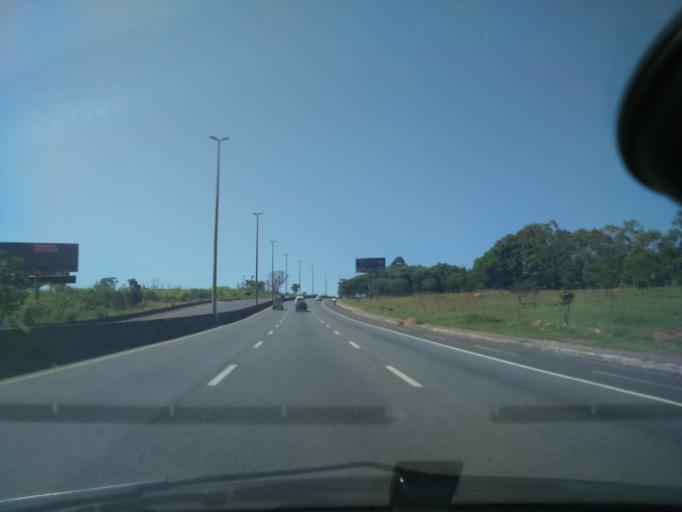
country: BR
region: Federal District
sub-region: Brasilia
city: Brasilia
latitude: -15.8432
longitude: -47.8204
